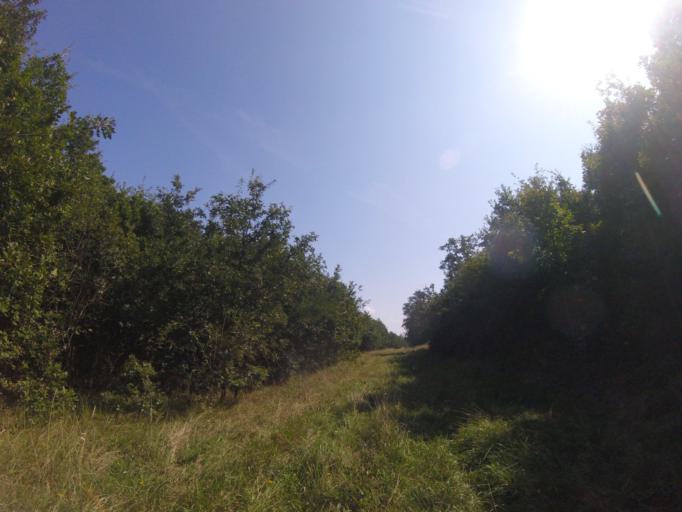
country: HU
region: Nograd
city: Bujak
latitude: 47.8957
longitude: 19.5144
